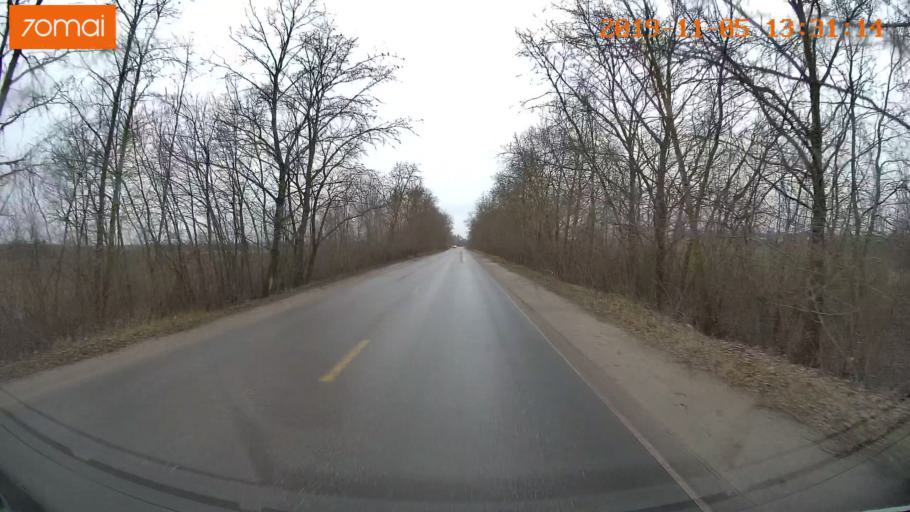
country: RU
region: Ivanovo
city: Shuya
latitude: 56.8736
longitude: 41.3926
